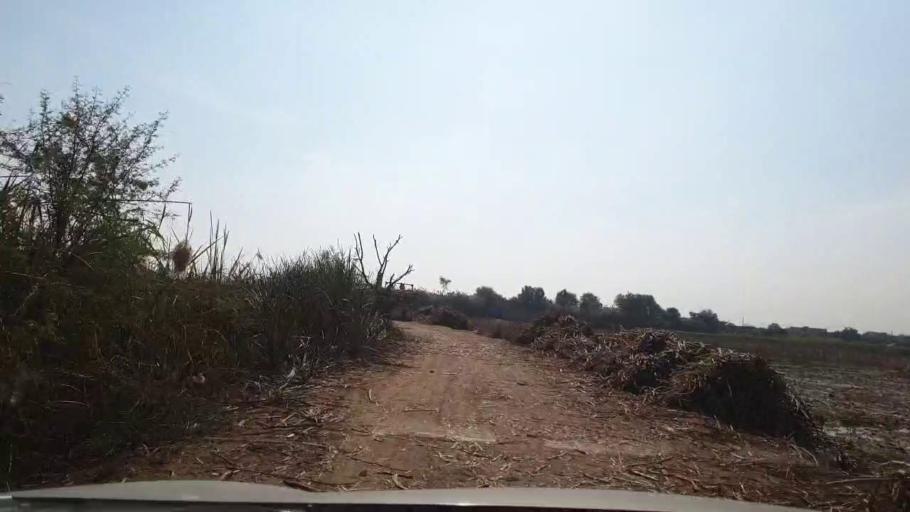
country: PK
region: Sindh
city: Berani
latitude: 25.7029
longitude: 68.7607
